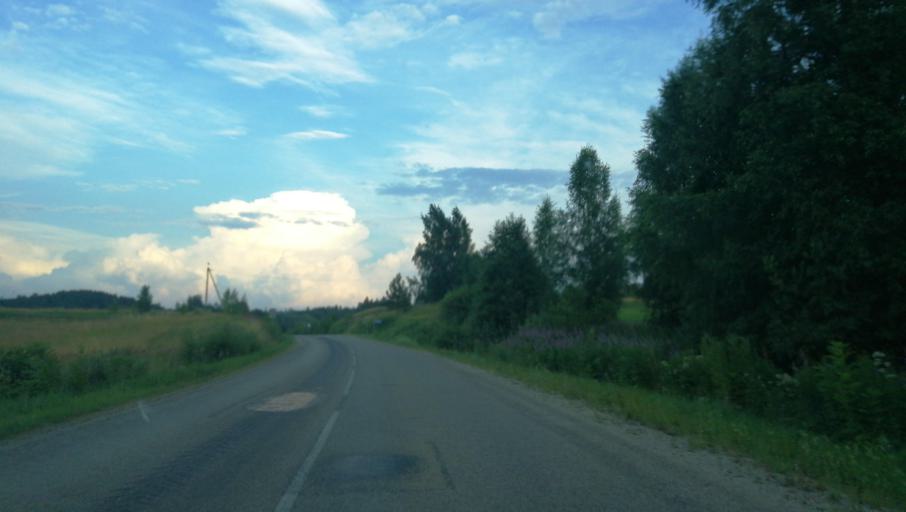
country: LV
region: Priekuli
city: Priekuli
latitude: 57.2609
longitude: 25.3590
